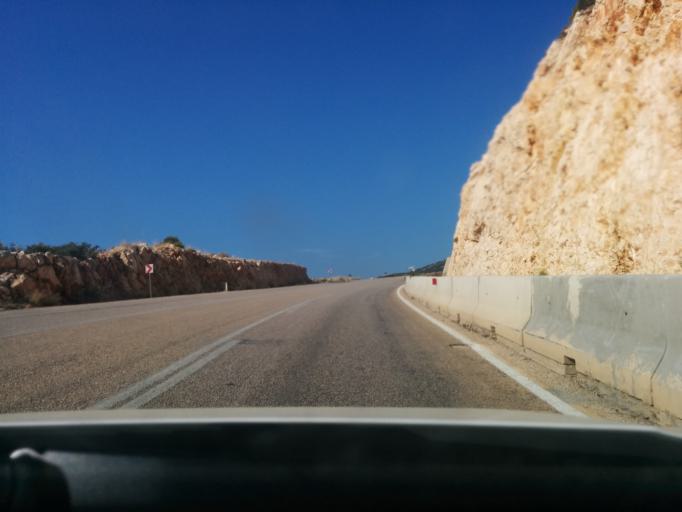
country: TR
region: Antalya
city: Kalkan
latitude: 36.2691
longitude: 29.4036
